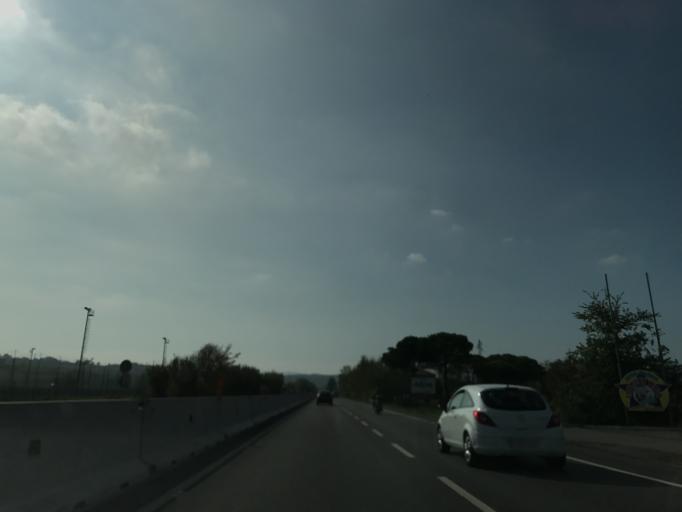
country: IT
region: Emilia-Romagna
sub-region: Provincia di Rimini
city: Cerasolo
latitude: 44.0108
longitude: 12.5458
